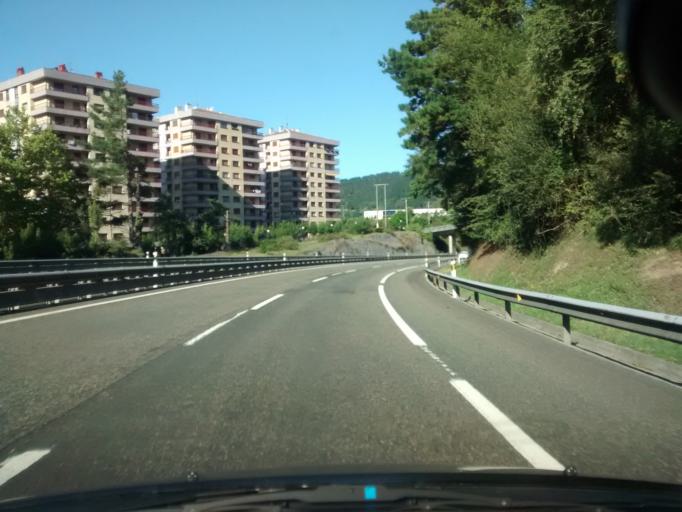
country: ES
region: Basque Country
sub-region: Provincia de Guipuzcoa
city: Elgoibar
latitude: 43.2123
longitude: -2.4150
